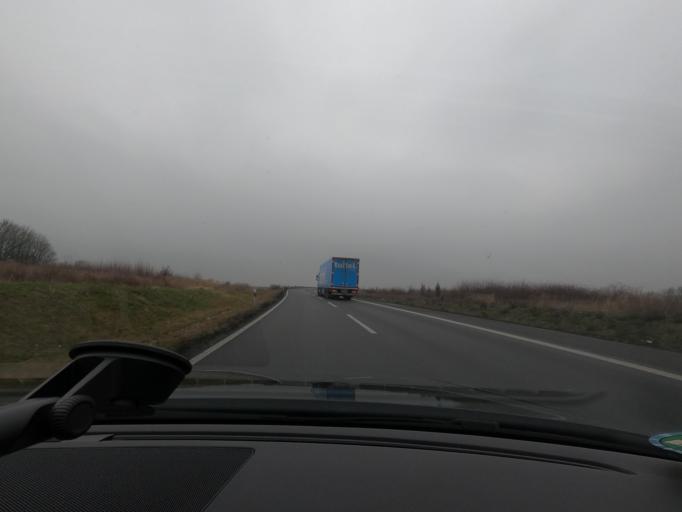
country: DE
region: North Rhine-Westphalia
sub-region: Regierungsbezirk Koln
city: Titz
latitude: 51.0303
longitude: 6.4791
